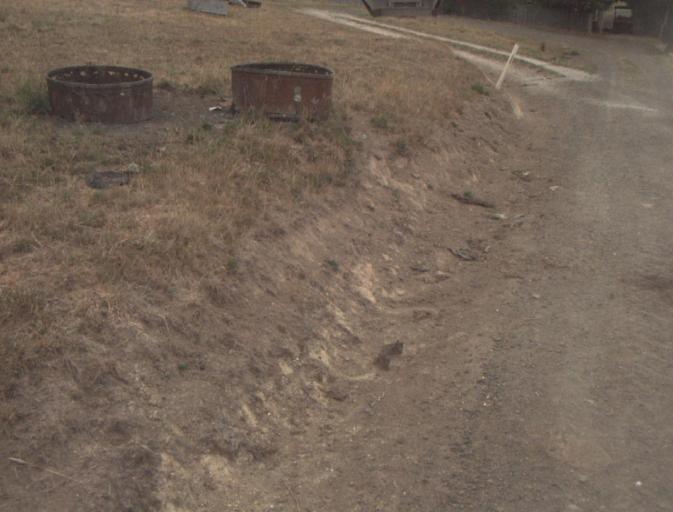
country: AU
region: Tasmania
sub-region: Launceston
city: Mayfield
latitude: -41.2408
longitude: 147.1858
